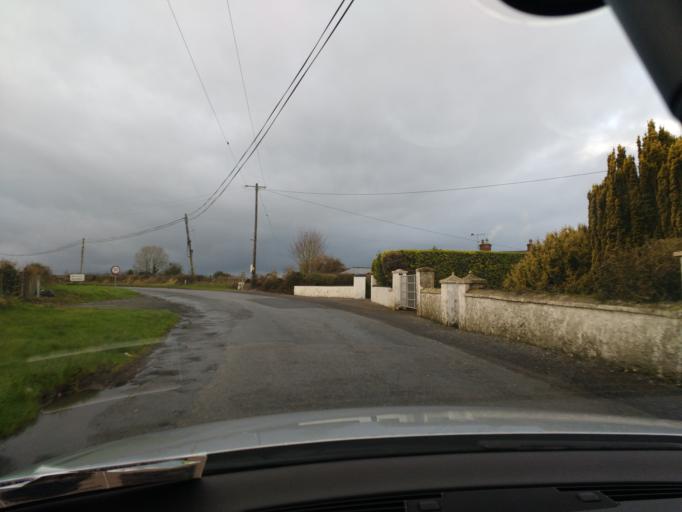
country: IE
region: Munster
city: Thurles
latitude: 52.6382
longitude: -7.8581
